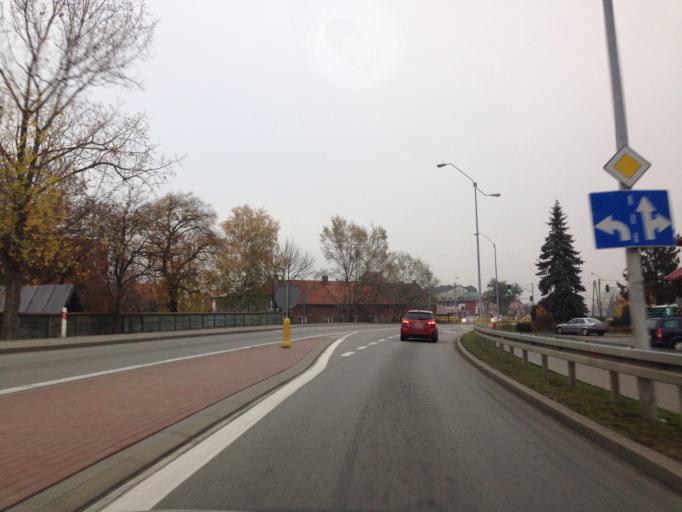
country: PL
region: Pomeranian Voivodeship
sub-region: Powiat gdanski
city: Pszczolki
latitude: 54.1737
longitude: 18.6965
